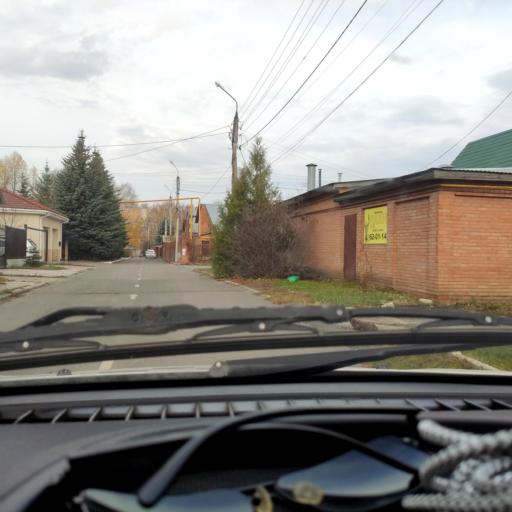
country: RU
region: Samara
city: Tol'yatti
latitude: 53.5369
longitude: 49.3874
